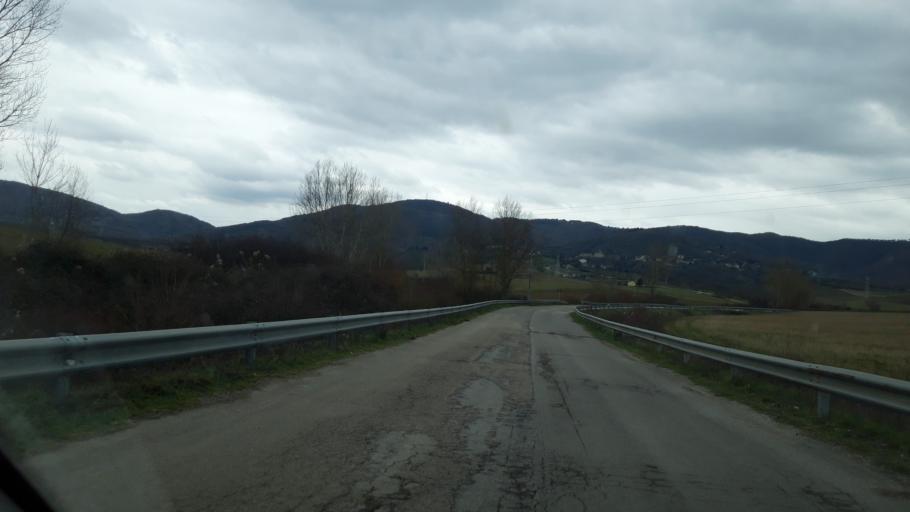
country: IT
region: Umbria
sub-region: Provincia di Perugia
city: Fontignano
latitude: 42.9931
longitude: 12.1872
